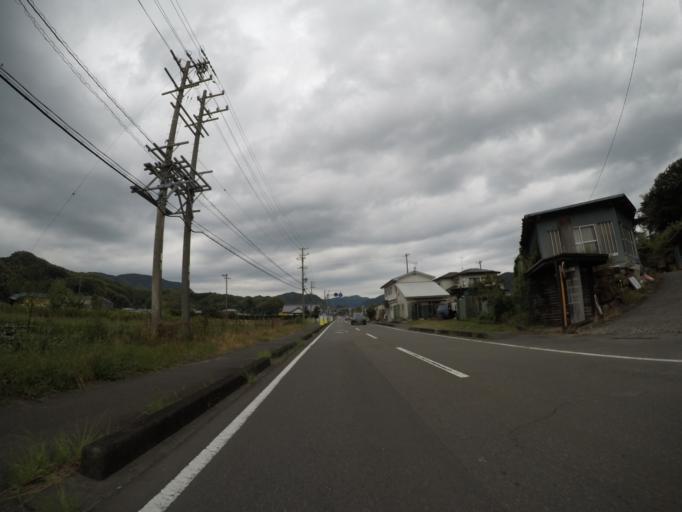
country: JP
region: Shizuoka
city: Fujieda
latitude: 34.9063
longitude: 138.2619
